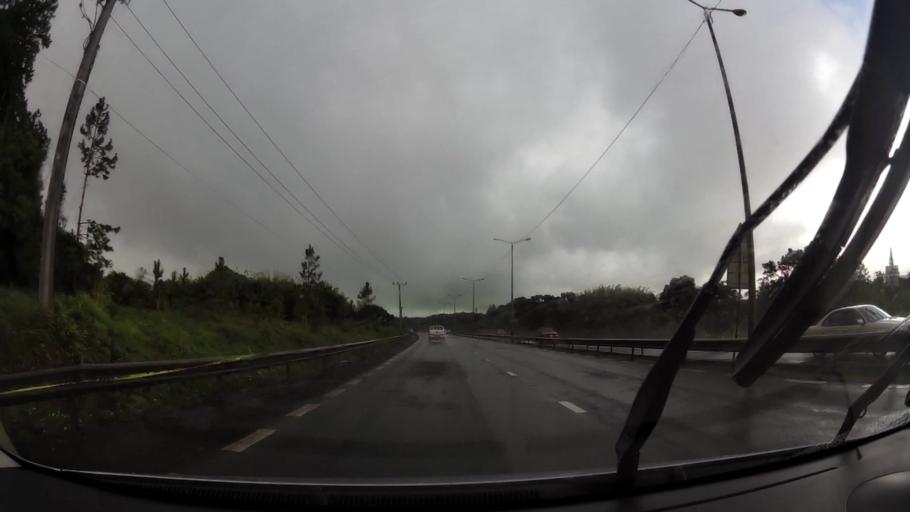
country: MU
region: Plaines Wilhems
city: Midlands
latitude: -20.3247
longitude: 57.5442
